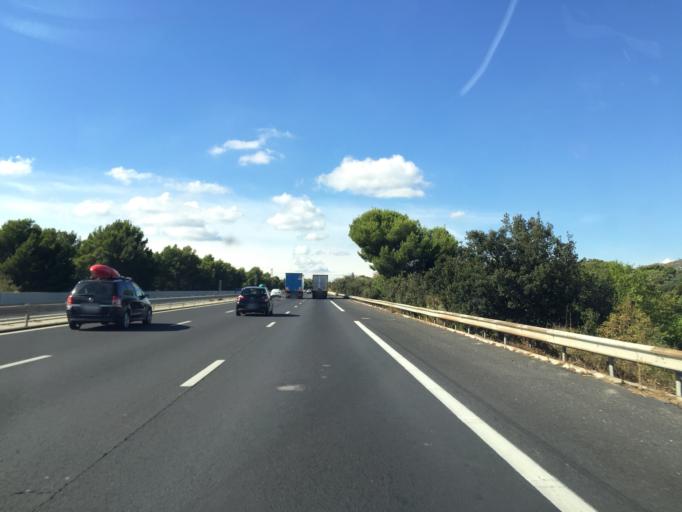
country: FR
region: Provence-Alpes-Cote d'Azur
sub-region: Departement des Bouches-du-Rhone
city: Pelissanne
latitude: 43.6311
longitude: 5.1242
